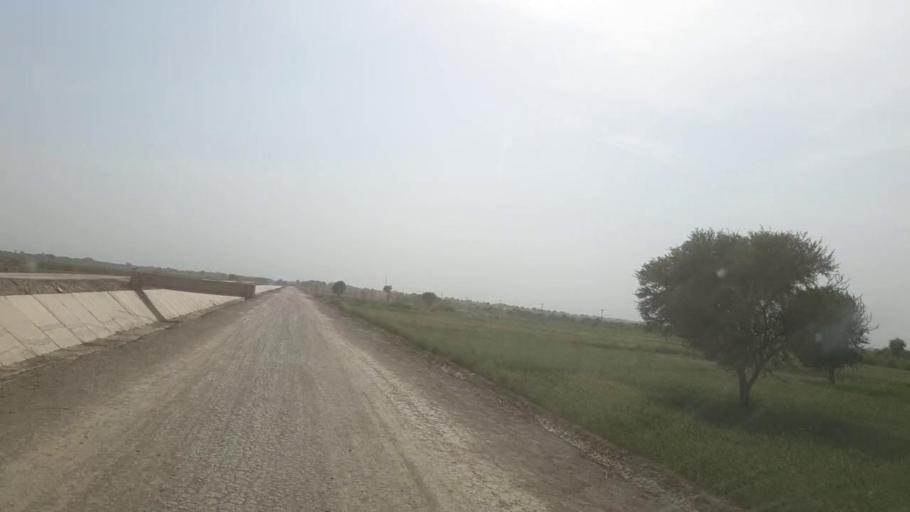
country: PK
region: Sindh
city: Nabisar
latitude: 25.0568
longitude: 69.5343
